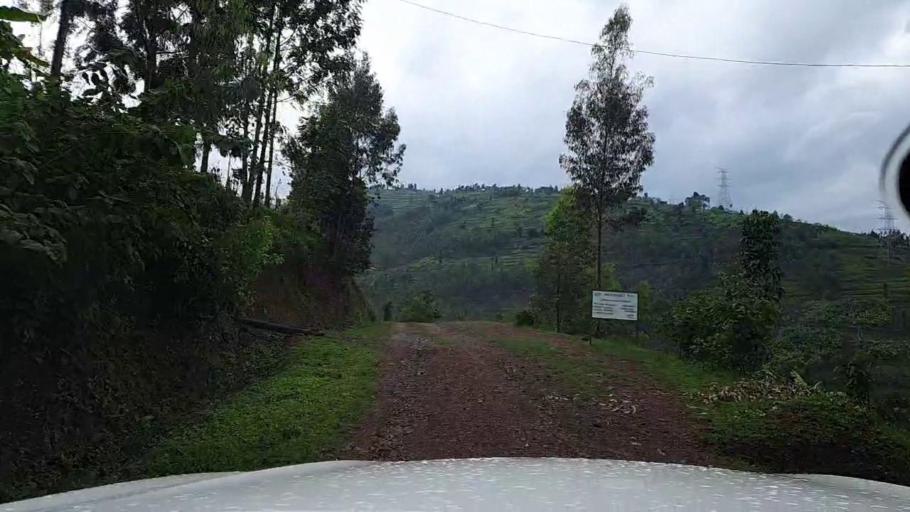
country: RW
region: Northern Province
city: Byumba
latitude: -1.7200
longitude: 29.9163
